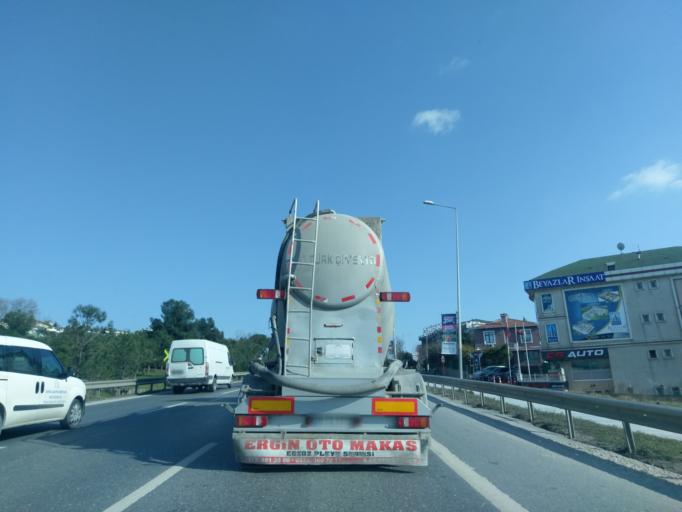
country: TR
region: Istanbul
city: Bueyuekcekmece
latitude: 41.0246
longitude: 28.5921
